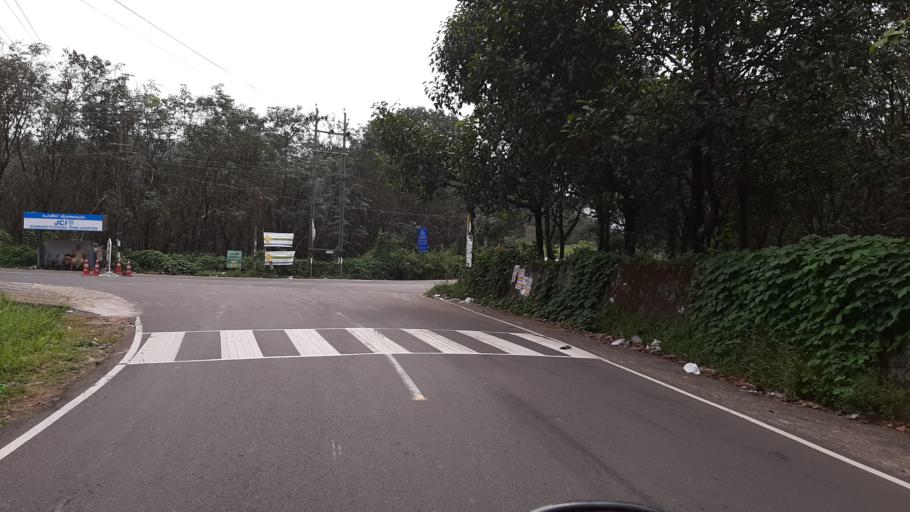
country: IN
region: Kerala
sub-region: Pattanamtitta
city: Pathanamthitta
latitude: 9.4552
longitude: 76.8666
